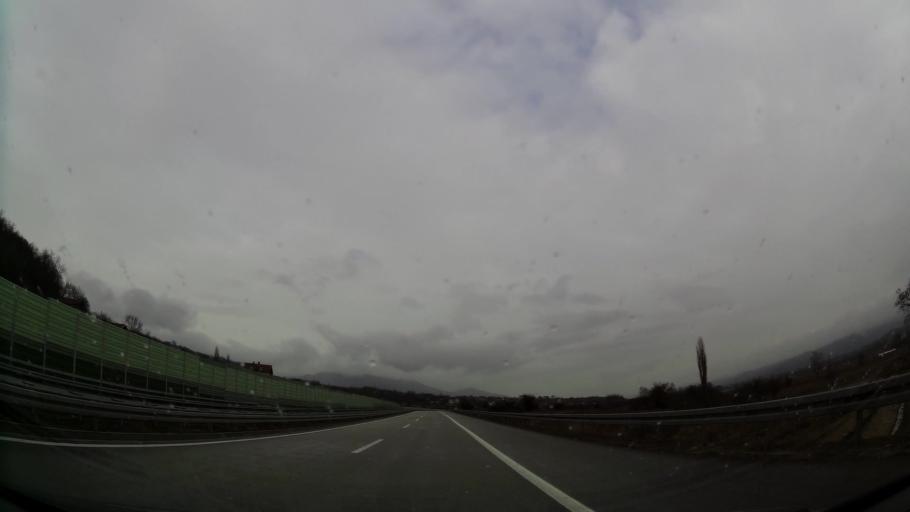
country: RS
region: Central Serbia
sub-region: Pcinjski Okrug
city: Vranjska Banja
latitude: 42.5593
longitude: 21.9508
